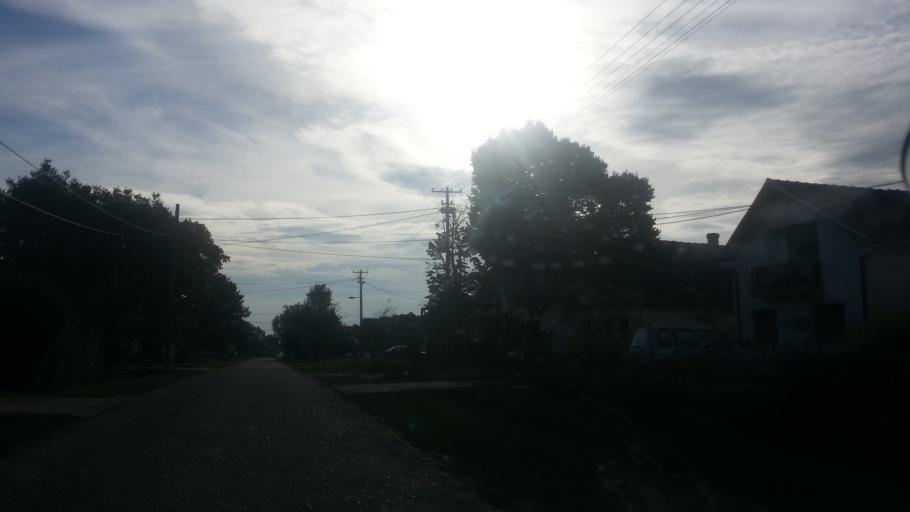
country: RS
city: Belegis
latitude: 45.0268
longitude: 20.3445
